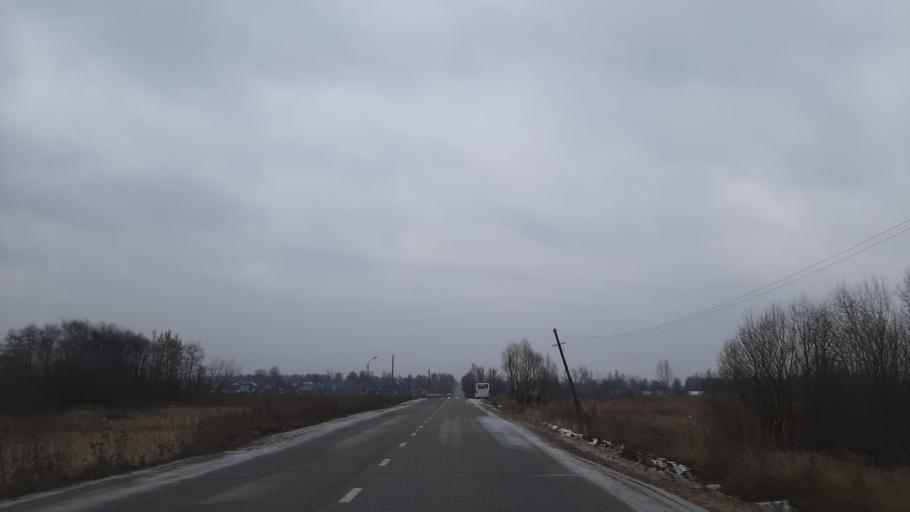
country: RU
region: Ivanovo
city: Shuya
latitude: 56.8796
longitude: 41.3449
